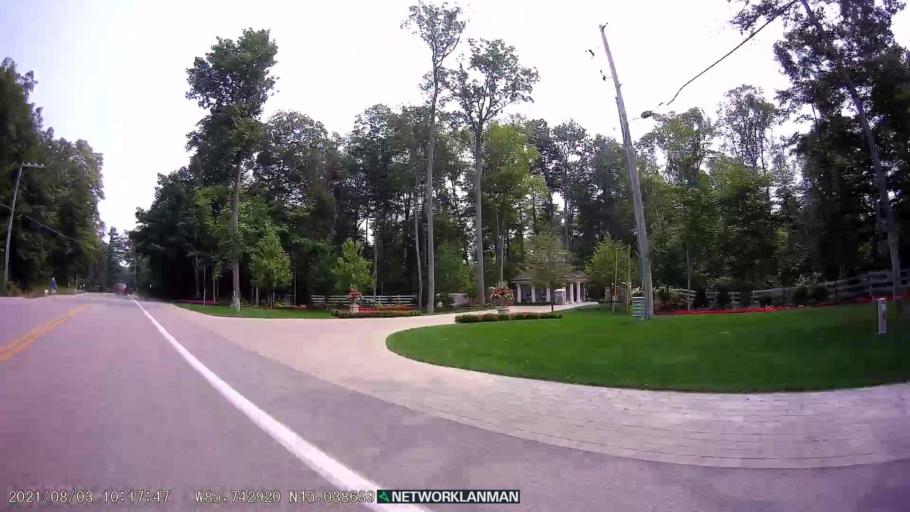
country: US
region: Michigan
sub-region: Leelanau County
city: Leland
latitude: 45.0430
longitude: -85.7391
